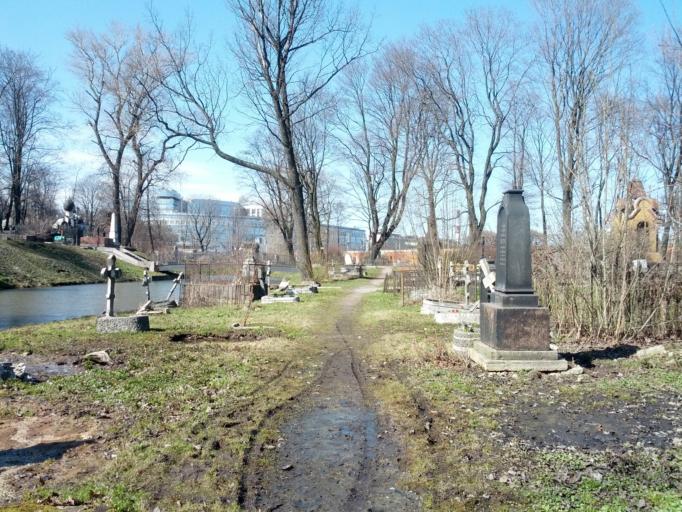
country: RU
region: St.-Petersburg
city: Centralniy
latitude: 59.9211
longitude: 30.3919
